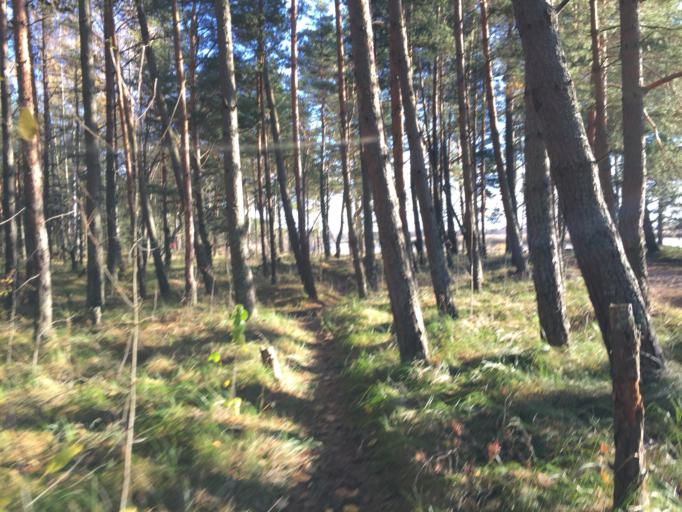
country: LV
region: Carnikava
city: Carnikava
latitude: 57.1587
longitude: 24.2697
